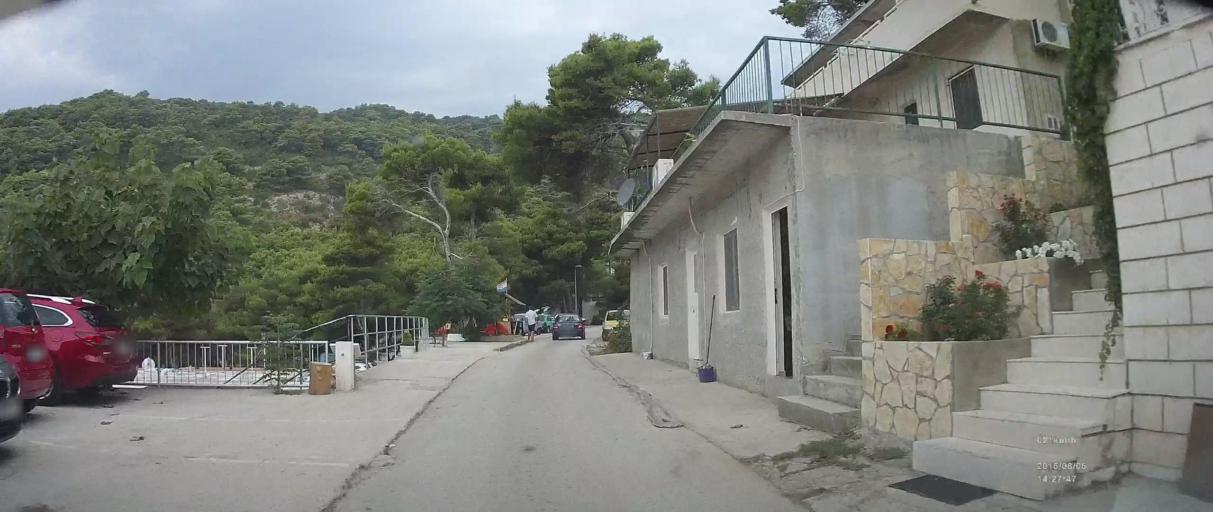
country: HR
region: Dubrovacko-Neretvanska
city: Ston
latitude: 42.7011
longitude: 17.7378
